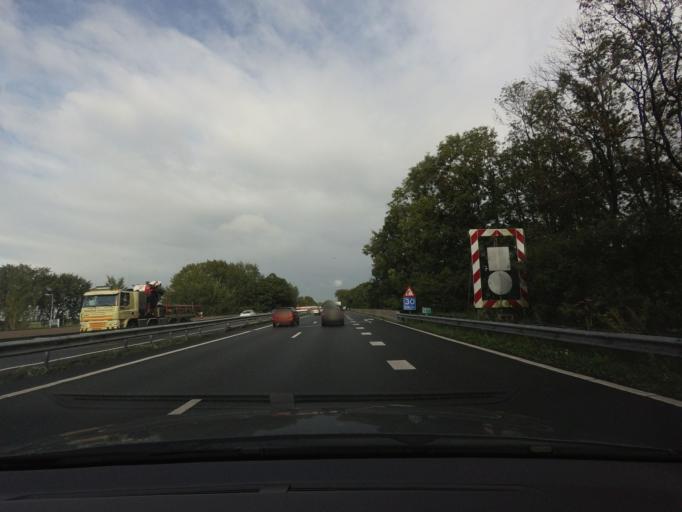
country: NL
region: South Holland
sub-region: Gemeente Teylingen
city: Sassenheim
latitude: 52.2211
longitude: 4.5410
